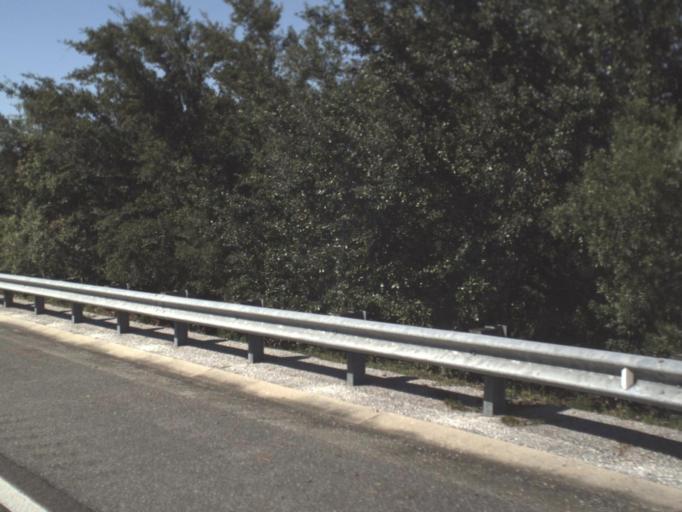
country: US
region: Florida
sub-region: Hillsborough County
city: Greater Northdale
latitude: 28.1266
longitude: -82.5344
